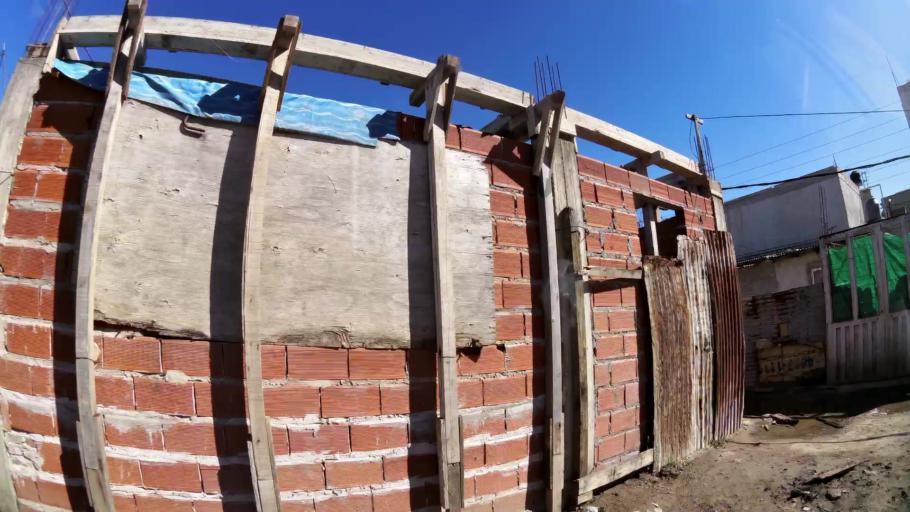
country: AR
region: Buenos Aires
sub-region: Partido de Quilmes
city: Quilmes
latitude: -34.7039
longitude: -58.3033
